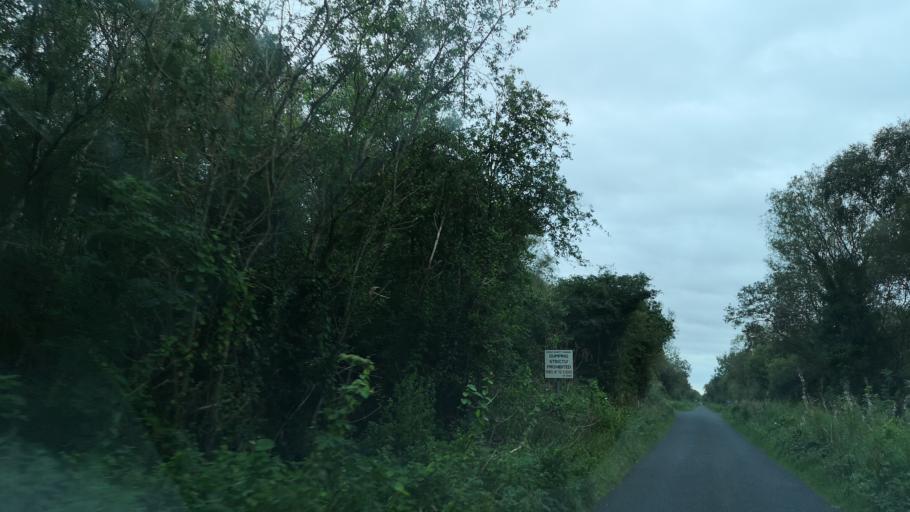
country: IE
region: Leinster
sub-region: Uibh Fhaili
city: Ferbane
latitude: 53.1973
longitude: -7.7254
